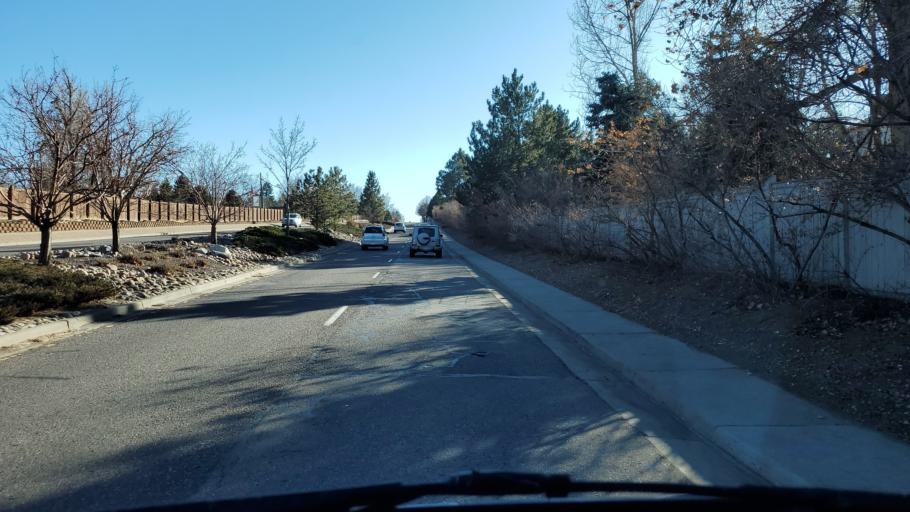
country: US
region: Colorado
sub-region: Arapahoe County
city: Castlewood
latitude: 39.5907
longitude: -104.9043
